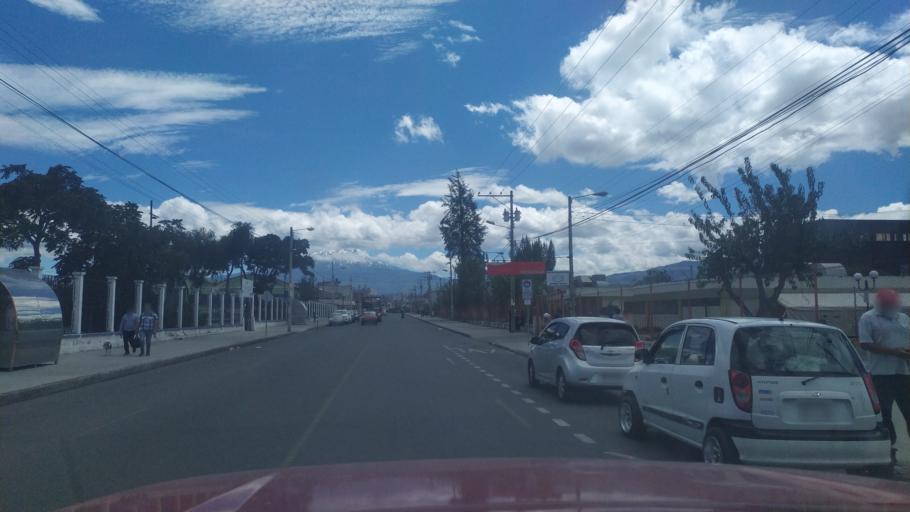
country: EC
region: Chimborazo
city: Riobamba
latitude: -1.6830
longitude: -78.6443
